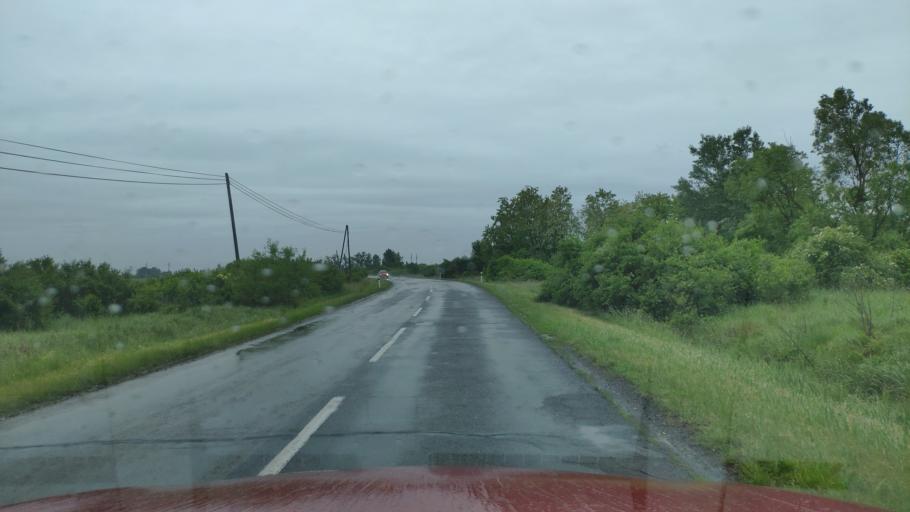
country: SK
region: Kosicky
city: Cierna nad Tisou
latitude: 48.4270
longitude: 22.0218
